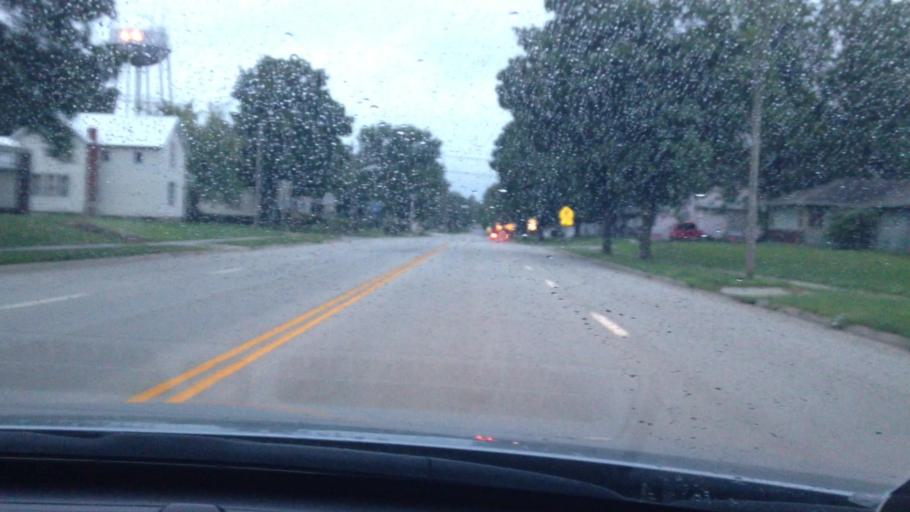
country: US
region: Kansas
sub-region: Brown County
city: Horton
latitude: 39.6698
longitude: -95.5273
